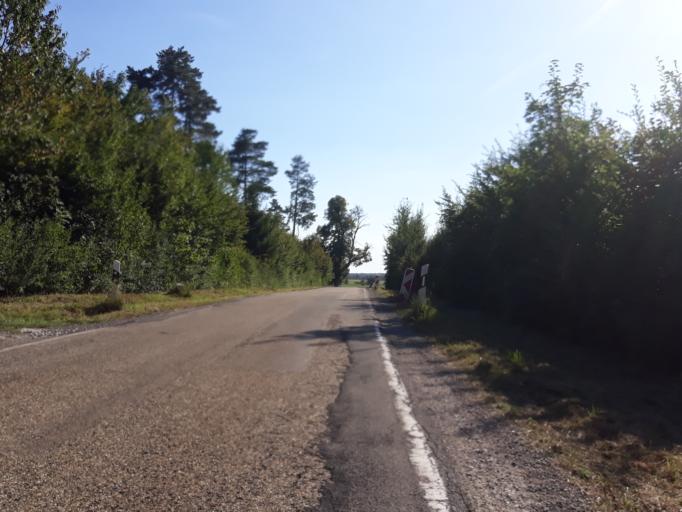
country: DE
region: Baden-Wuerttemberg
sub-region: Regierungsbezirk Stuttgart
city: Deckenpfronn
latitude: 48.6658
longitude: 8.8419
